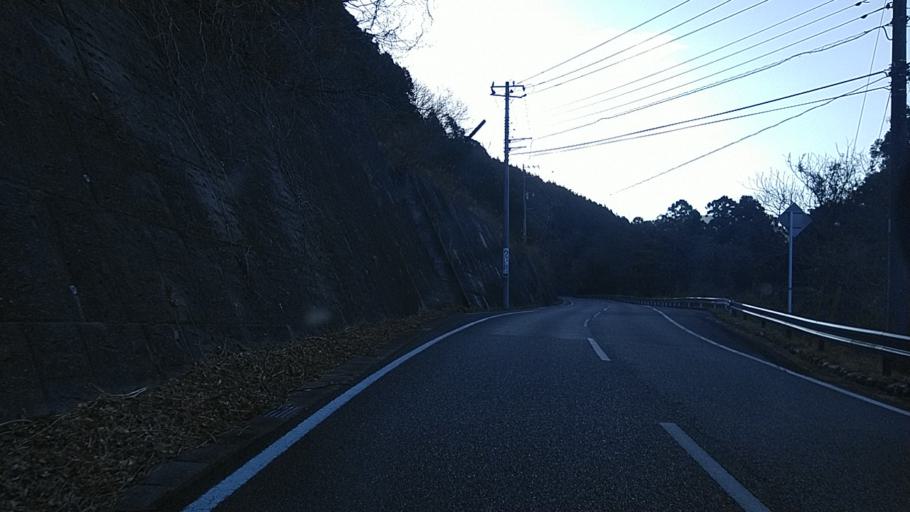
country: JP
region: Chiba
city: Kimitsu
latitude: 35.2612
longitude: 139.9329
